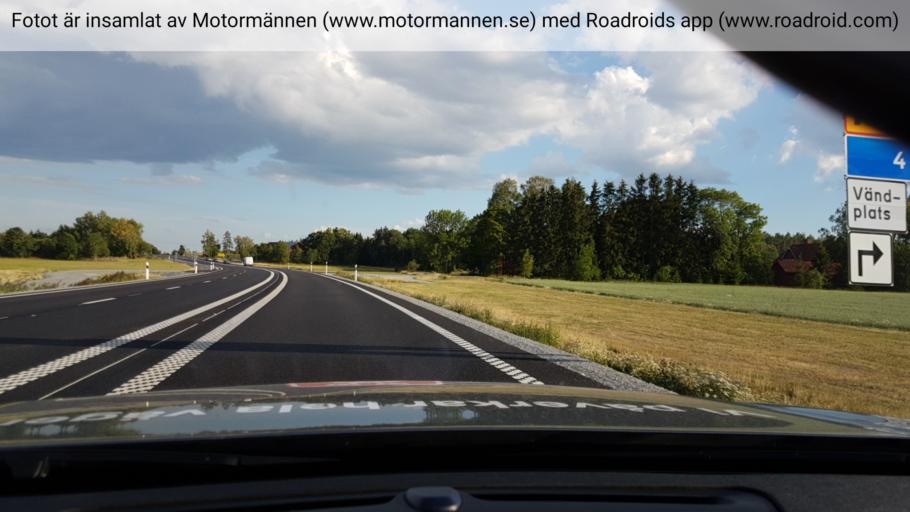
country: SE
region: Uppsala
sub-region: Enkopings Kommun
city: Irsta
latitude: 59.7263
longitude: 16.9584
